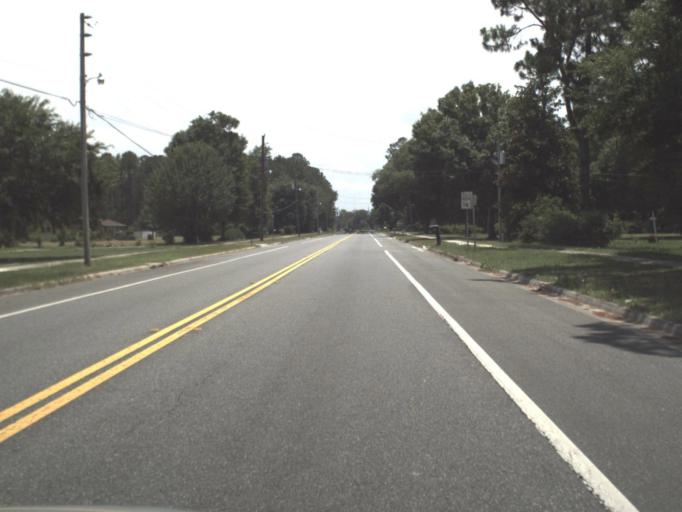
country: US
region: Florida
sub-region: Bradford County
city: Starke
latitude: 29.9664
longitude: -82.1196
